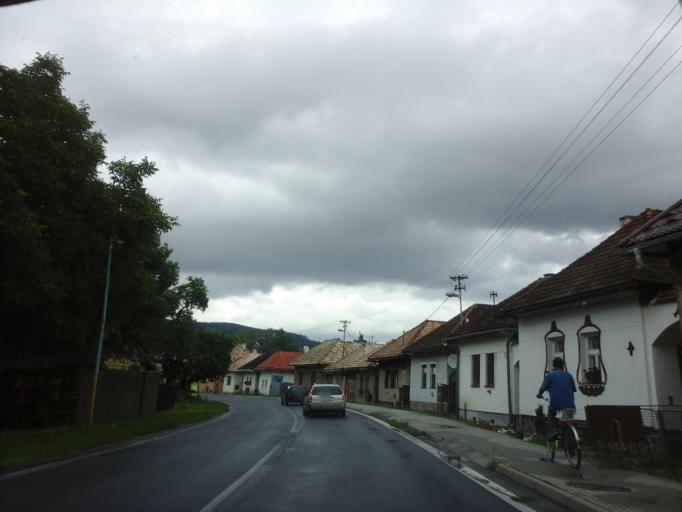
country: SK
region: Presovsky
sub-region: Okres Poprad
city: Poprad
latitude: 48.9886
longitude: 20.3091
